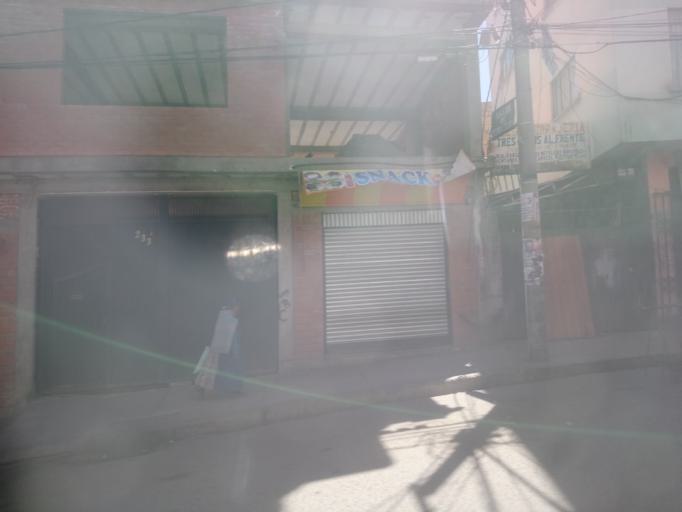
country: BO
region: La Paz
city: La Paz
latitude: -16.5010
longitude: -68.1052
